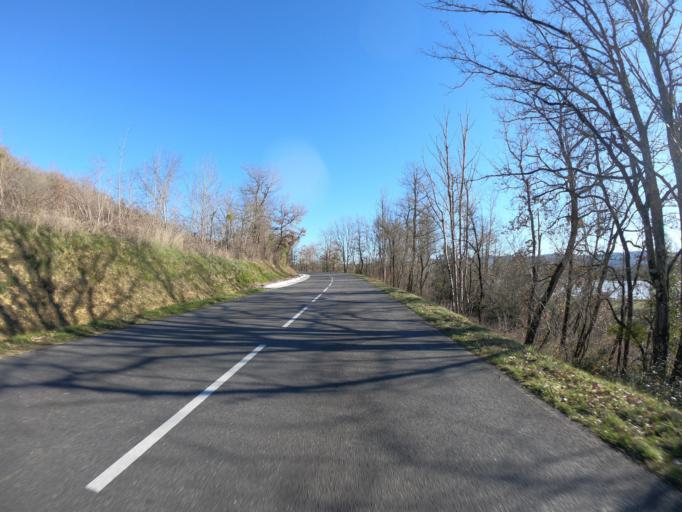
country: FR
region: Midi-Pyrenees
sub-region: Departement de l'Ariege
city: Mirepoix
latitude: 43.0847
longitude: 1.8020
